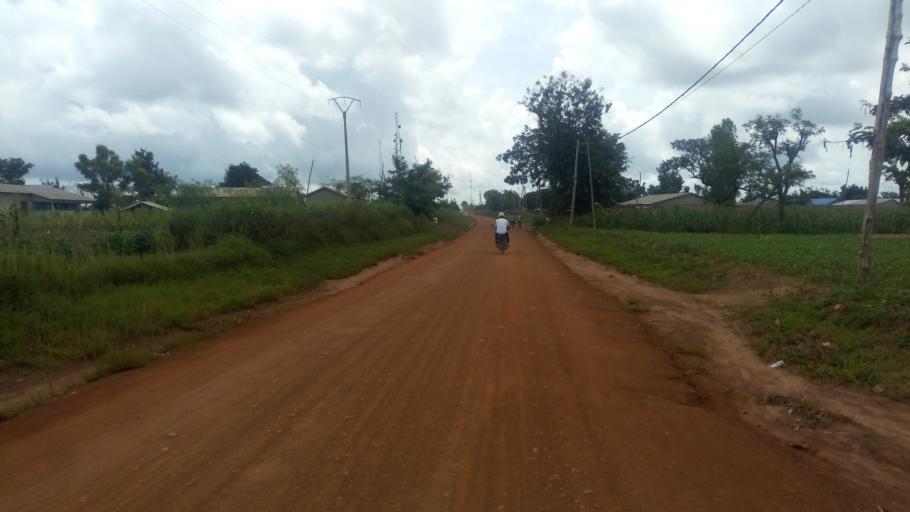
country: TG
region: Centrale
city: Sotouboua
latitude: 8.5566
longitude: 0.9988
